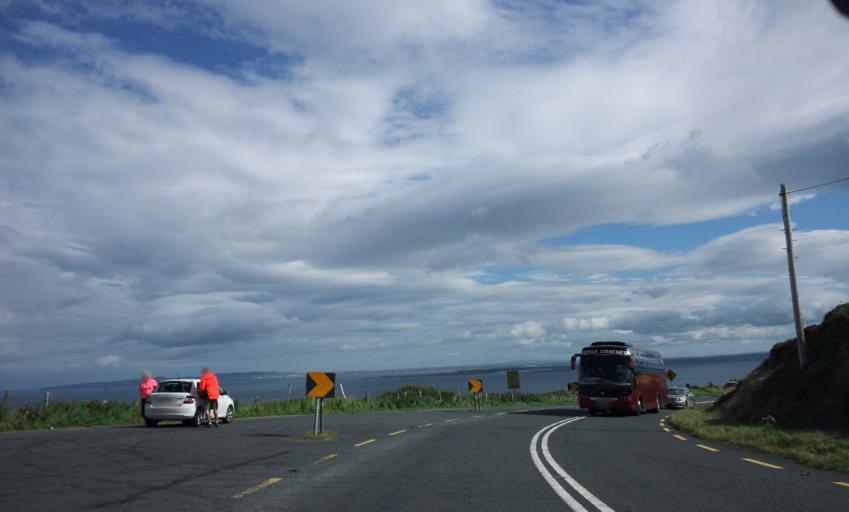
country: IE
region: Munster
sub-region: Ciarrai
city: Killorglin
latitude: 52.2149
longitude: -9.9404
